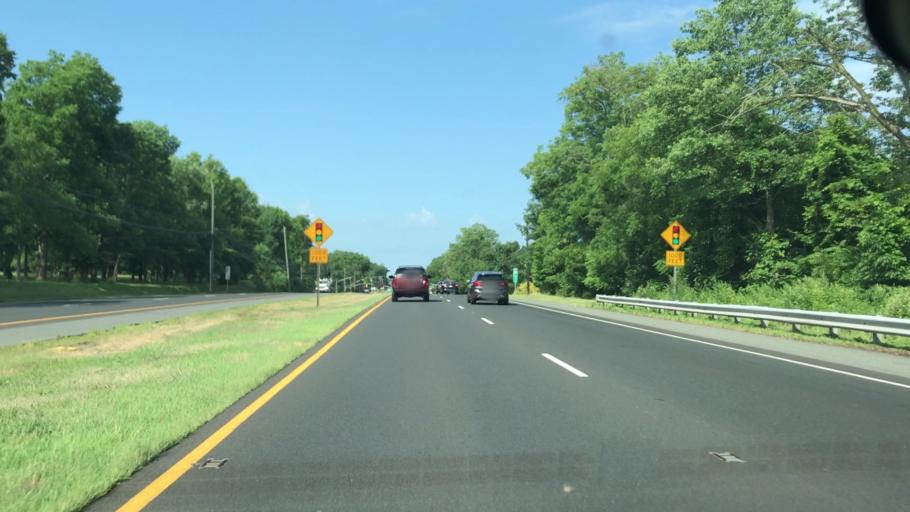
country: US
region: New Jersey
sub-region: Hunterdon County
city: Flemington
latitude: 40.5173
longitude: -74.8172
